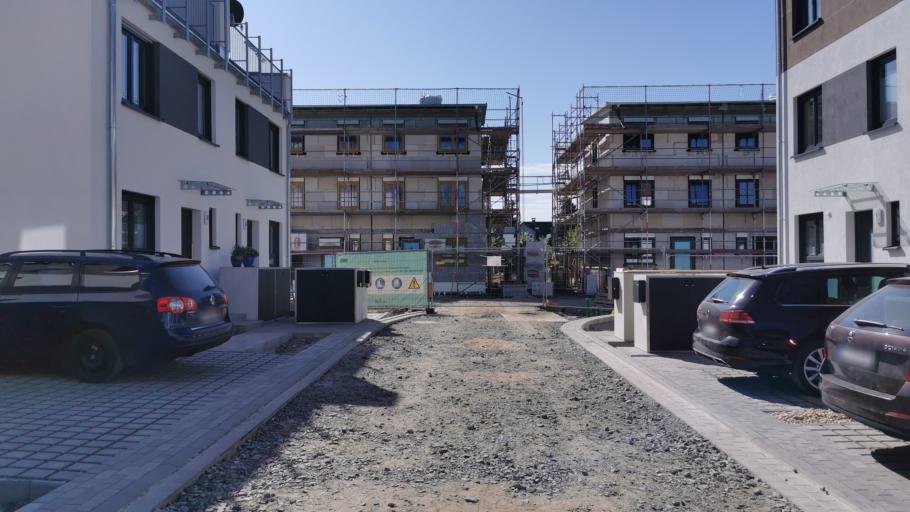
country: DE
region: Saxony
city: Markranstadt
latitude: 51.3053
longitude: 12.2305
